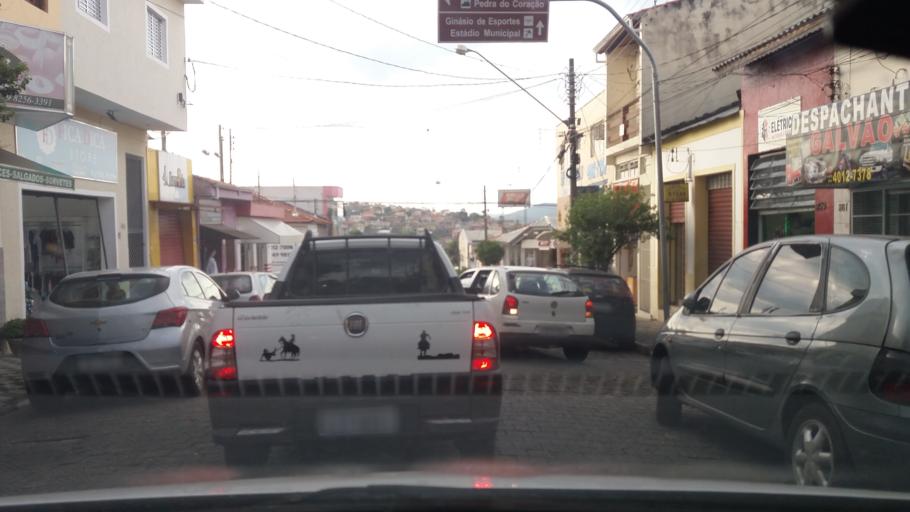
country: BR
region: Sao Paulo
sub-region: Bom Jesus Dos Perdoes
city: Bom Jesus dos Perdoes
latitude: -23.1350
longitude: -46.4651
